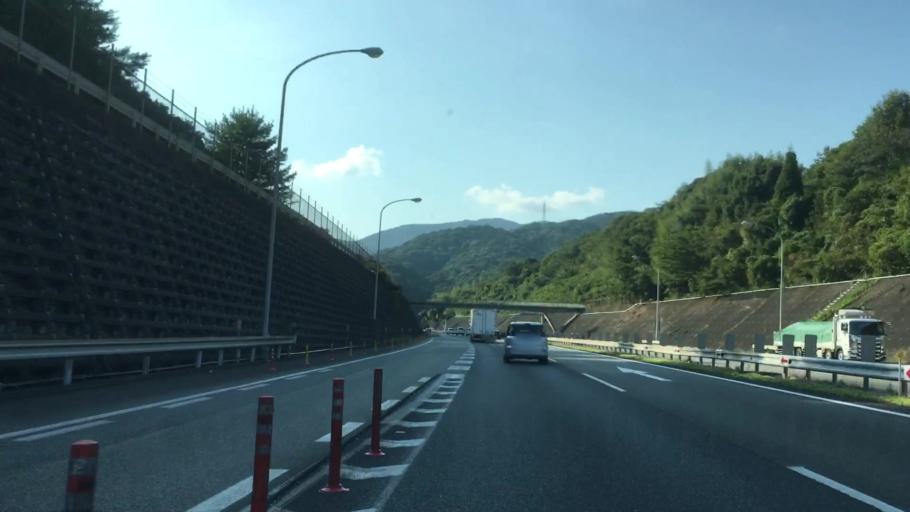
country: JP
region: Yamaguchi
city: Hofu
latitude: 34.0705
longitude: 131.6839
